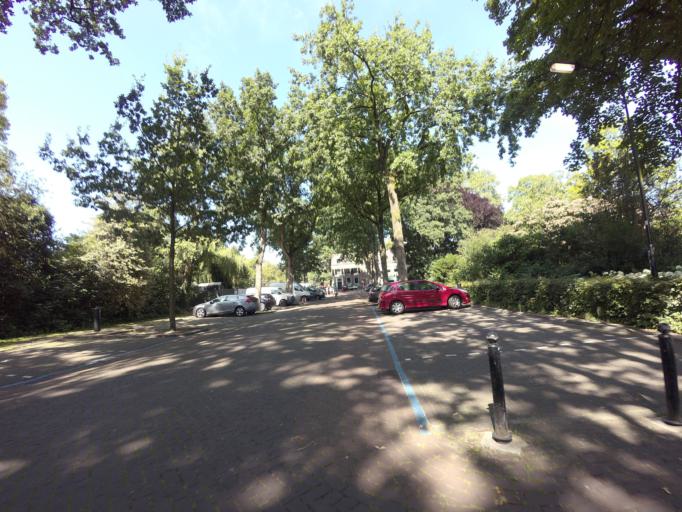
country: NL
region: North Holland
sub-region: Gemeente Amsterdam
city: Amsterdam-Zuidoost
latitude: 52.2708
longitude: 4.9756
